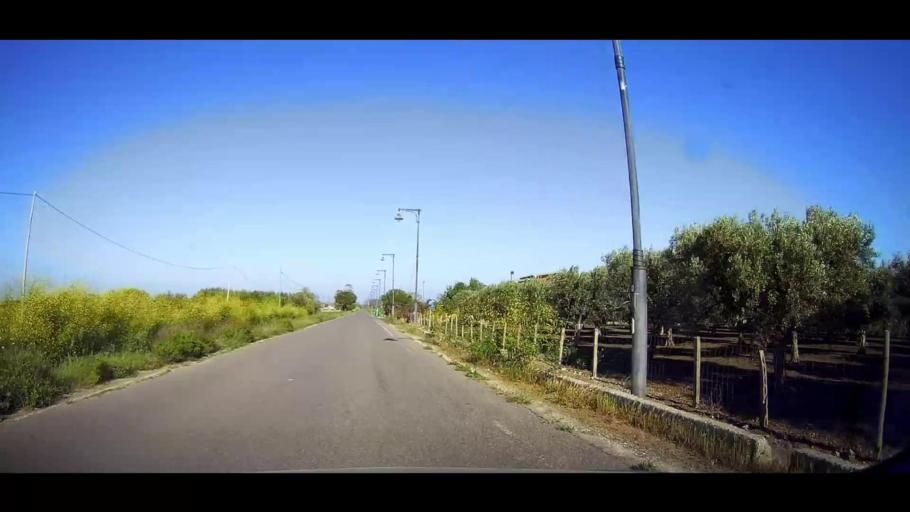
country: IT
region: Calabria
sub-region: Provincia di Crotone
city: Crotone
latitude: 39.0249
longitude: 17.1767
